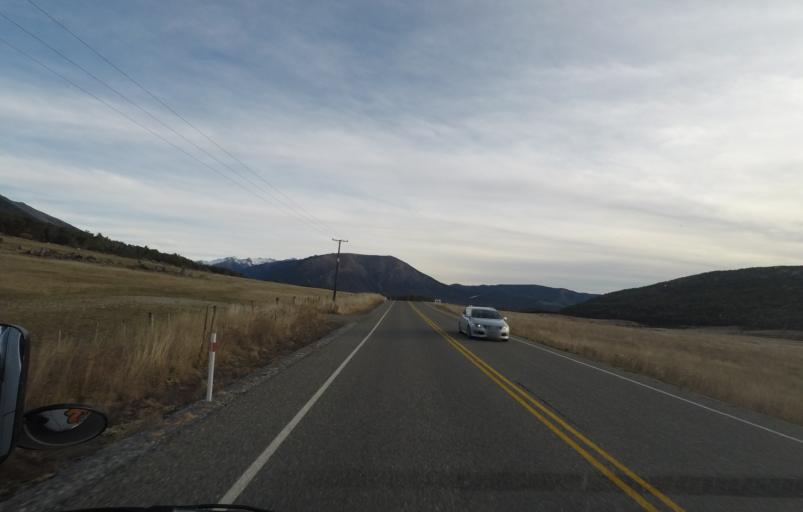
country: NZ
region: Tasman
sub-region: Tasman District
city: Wakefield
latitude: -41.7956
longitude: 172.8745
